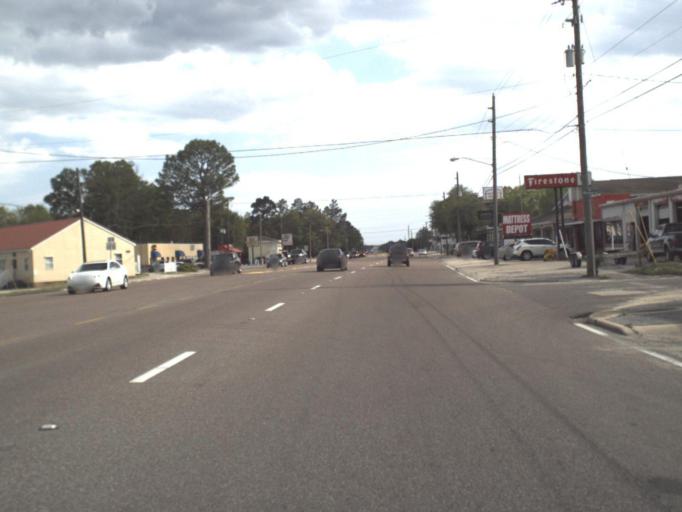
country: US
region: Florida
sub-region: Okaloosa County
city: Valparaiso
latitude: 30.5097
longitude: -86.4938
